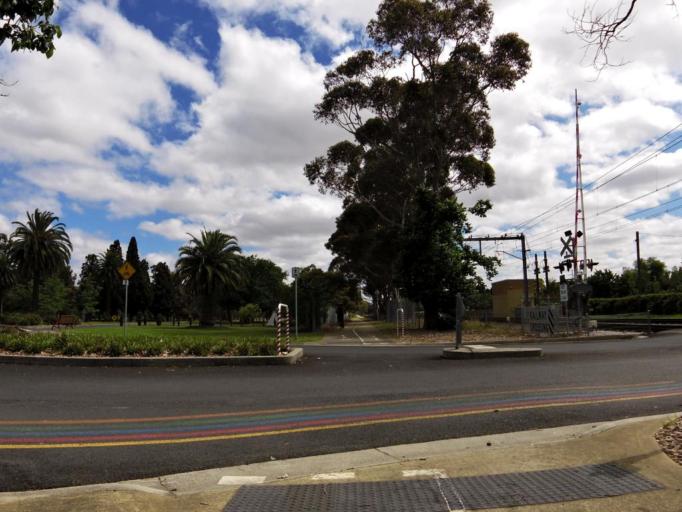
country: AU
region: Victoria
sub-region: Moreland
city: Fawkner
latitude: -37.7136
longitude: 144.9602
